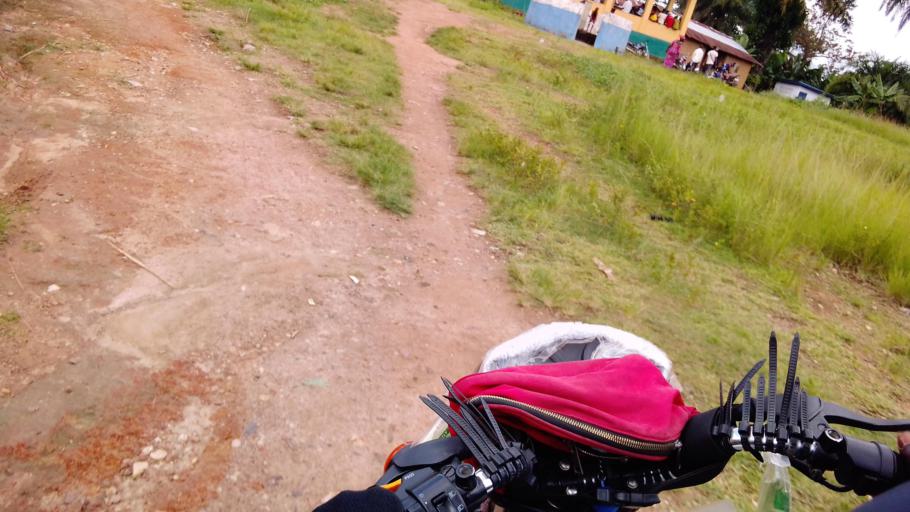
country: SL
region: Eastern Province
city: Koidu
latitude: 8.6756
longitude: -10.9771
